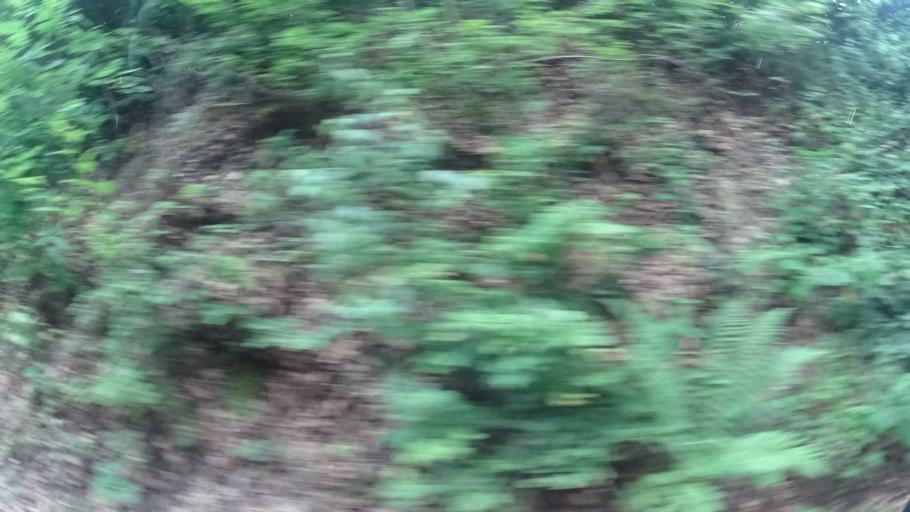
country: DE
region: Bavaria
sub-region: Regierungsbezirk Unterfranken
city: Johannesberg
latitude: 50.0724
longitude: 9.1173
